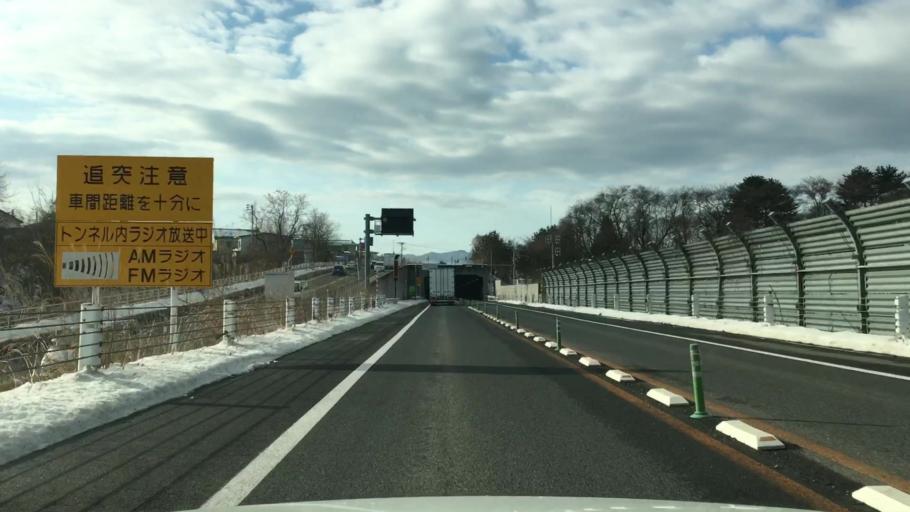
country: JP
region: Akita
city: Odate
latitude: 40.2780
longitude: 140.5364
